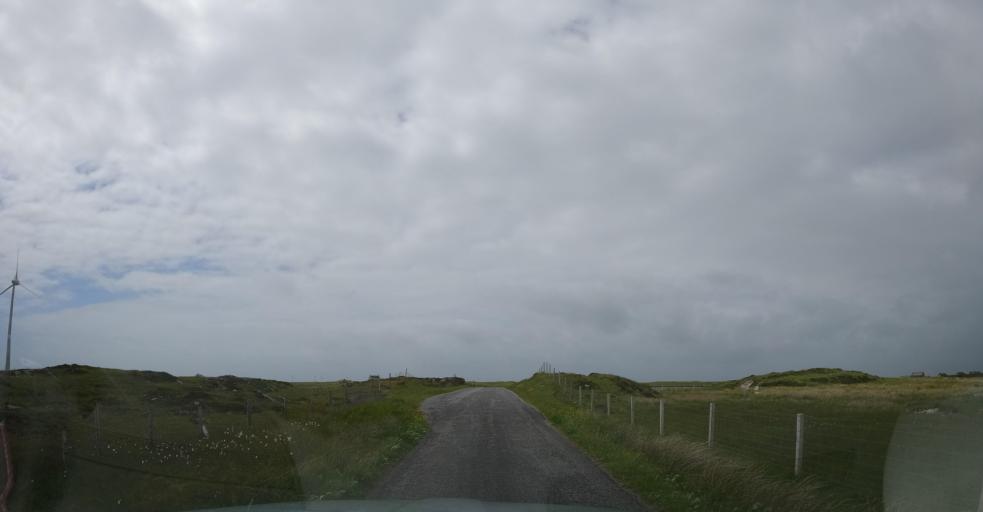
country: GB
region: Scotland
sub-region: Eilean Siar
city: Isle of South Uist
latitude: 57.2418
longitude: -7.4021
